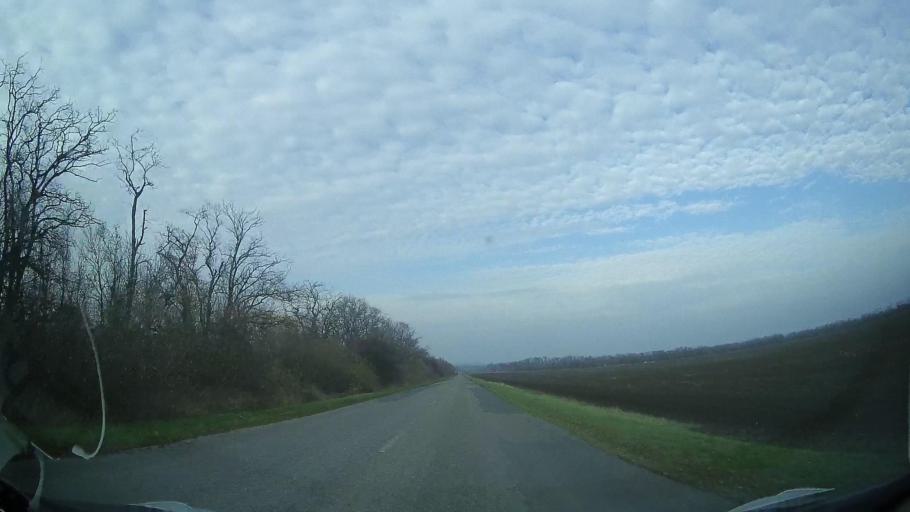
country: RU
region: Rostov
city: Bagayevskaya
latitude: 47.0861
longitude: 40.3915
